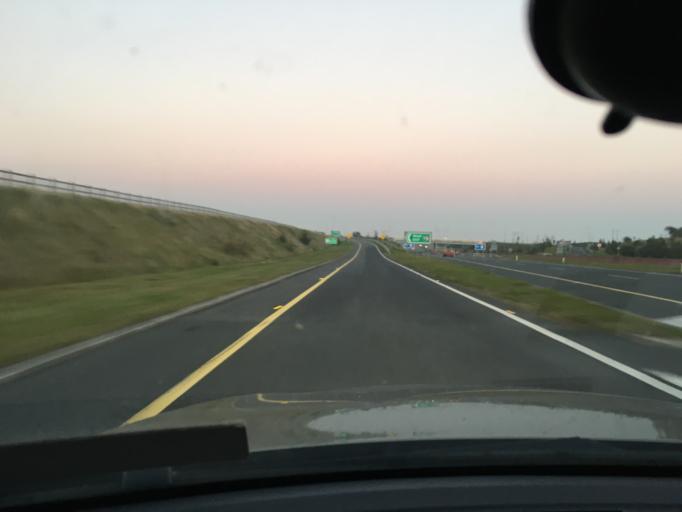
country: IE
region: Connaught
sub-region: County Galway
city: Oranmore
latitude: 53.2954
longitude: -8.9294
